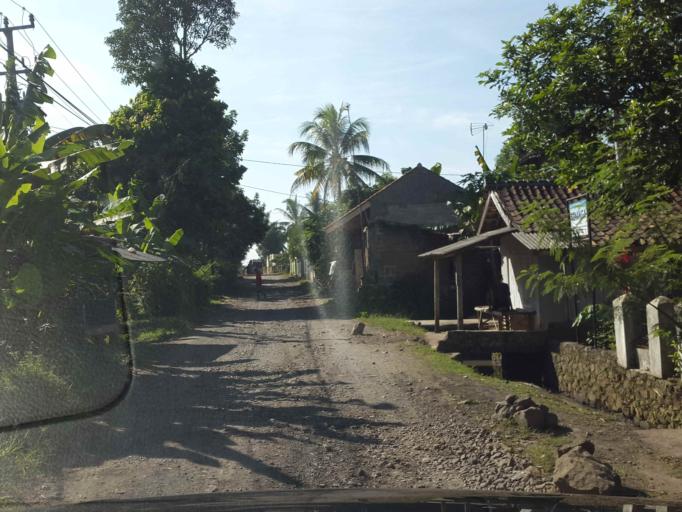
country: ID
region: West Java
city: Ciranjang-hilir
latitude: -6.8212
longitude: 107.2260
